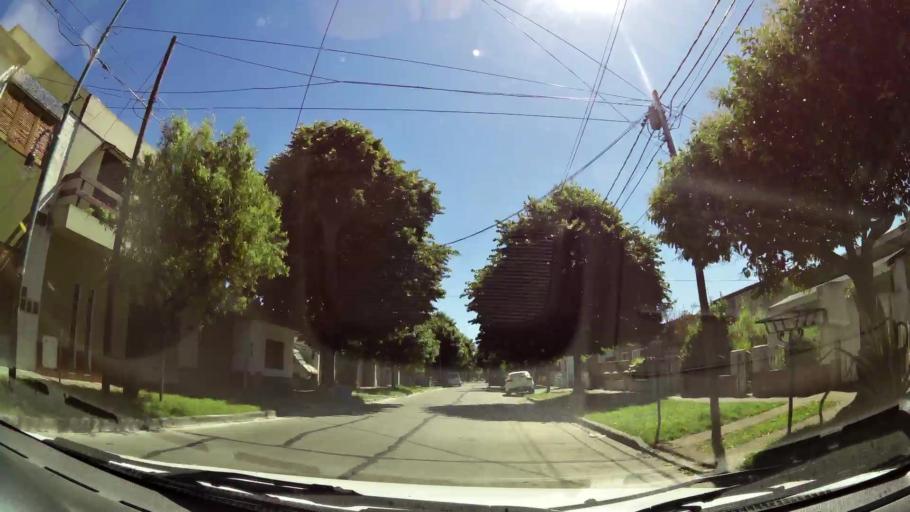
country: AR
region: Buenos Aires
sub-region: Partido de General San Martin
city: General San Martin
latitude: -34.5225
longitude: -58.5360
